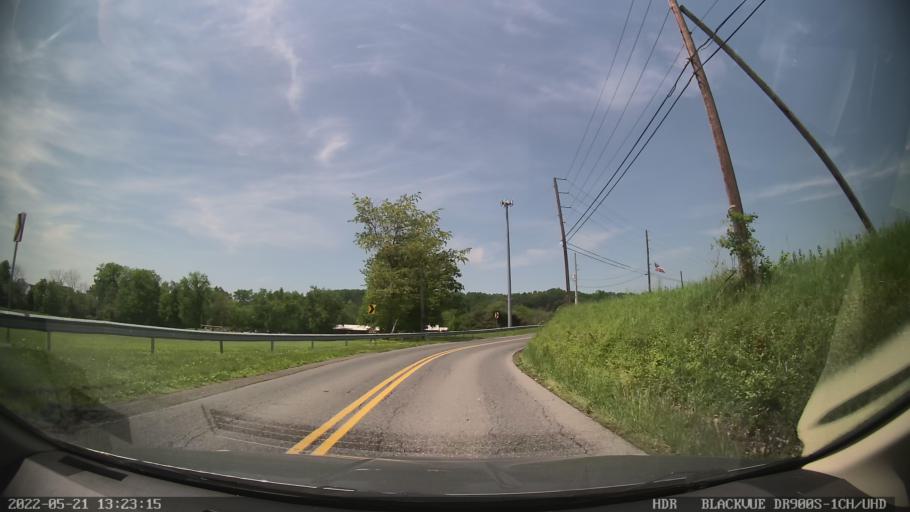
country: US
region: Pennsylvania
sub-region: Berks County
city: Bally
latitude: 40.3880
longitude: -75.6094
